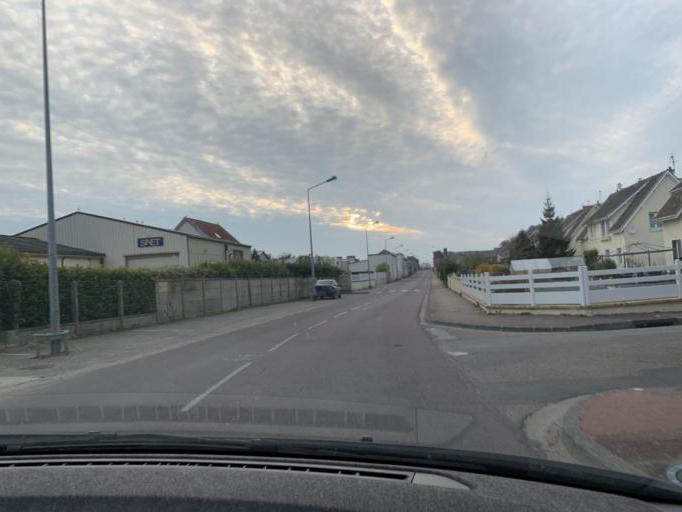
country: FR
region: Haute-Normandie
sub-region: Departement de la Seine-Maritime
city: Fecamp
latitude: 49.7570
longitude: 0.3969
